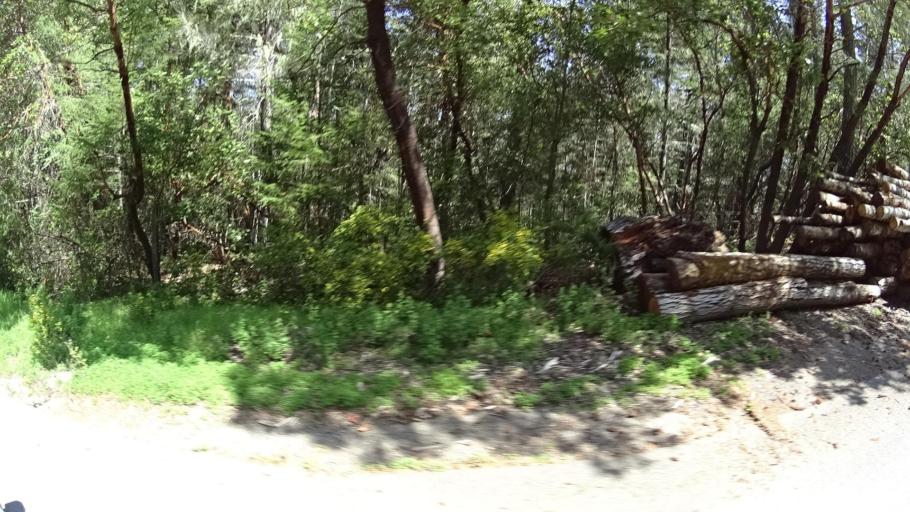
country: US
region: California
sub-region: Humboldt County
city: Redway
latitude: 40.1436
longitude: -123.6296
